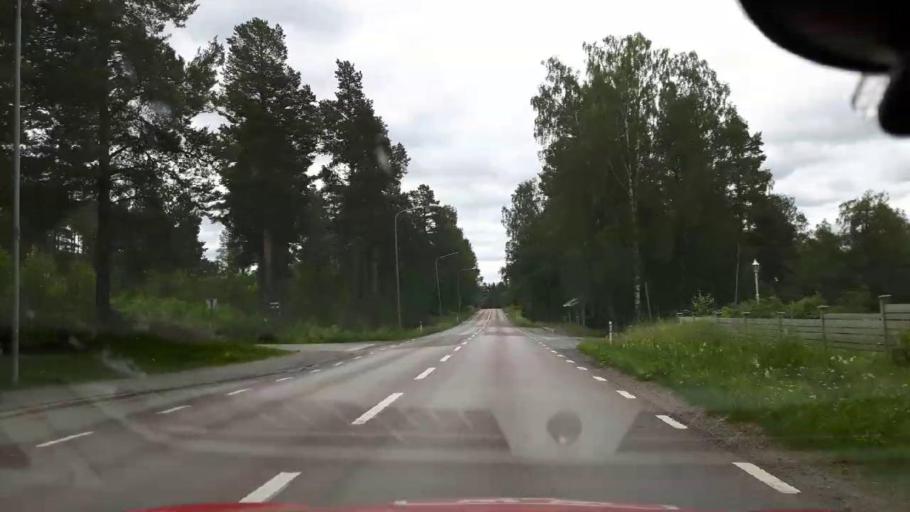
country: SE
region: Jaemtland
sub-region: OEstersunds Kommun
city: Brunflo
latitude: 62.9530
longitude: 15.0474
